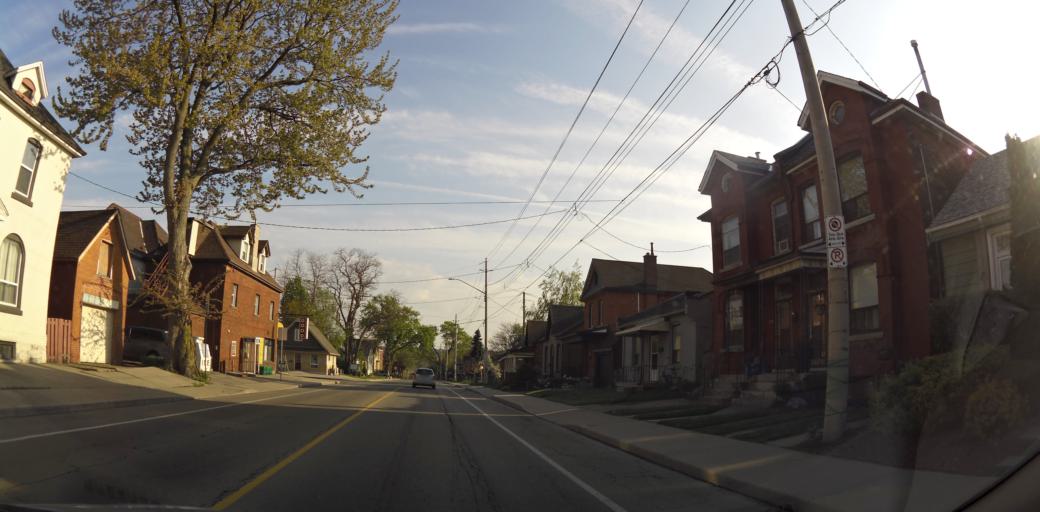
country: CA
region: Ontario
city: Hamilton
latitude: 43.2667
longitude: -79.8860
